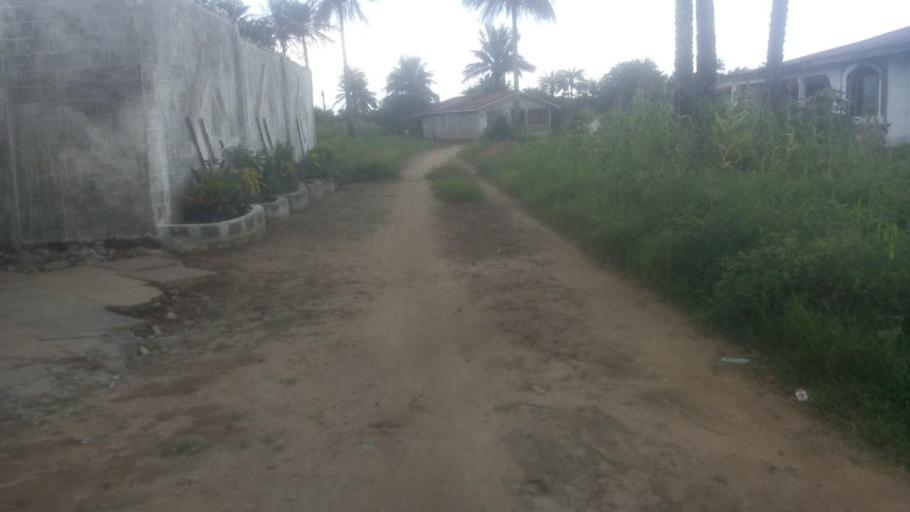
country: SL
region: Northern Province
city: Masoyila
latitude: 8.5780
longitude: -13.1665
